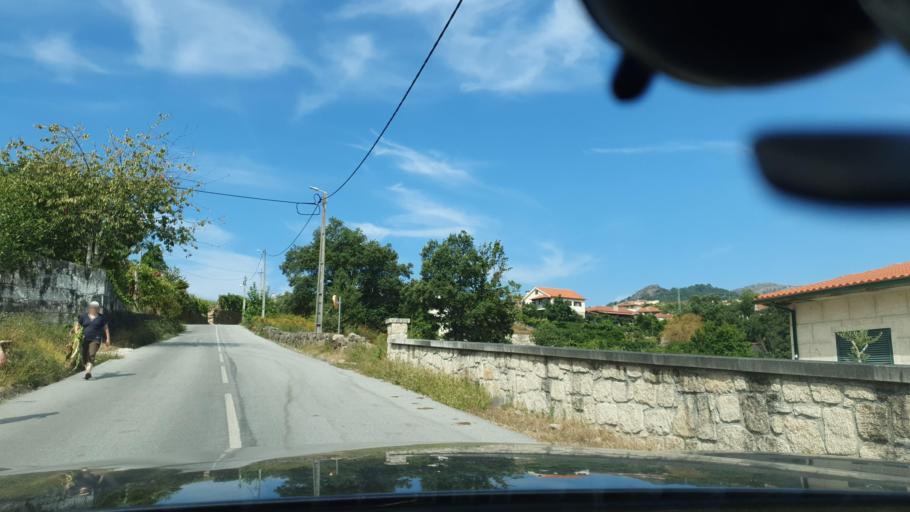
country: PT
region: Braga
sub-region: Vieira do Minho
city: Vieira do Minho
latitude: 41.7005
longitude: -8.0865
